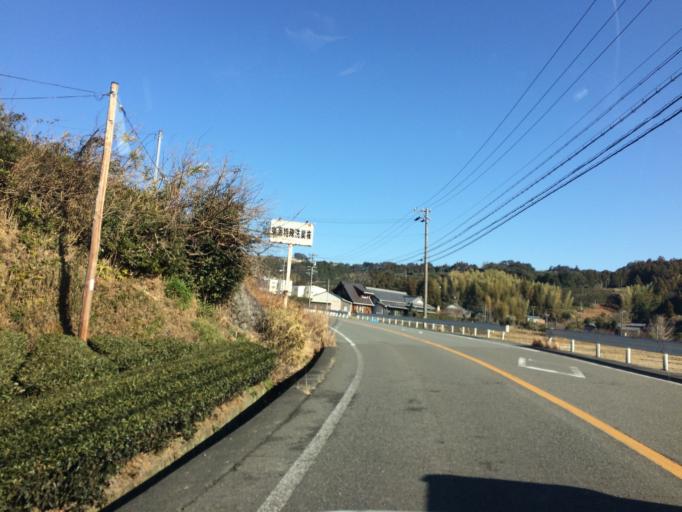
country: JP
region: Shizuoka
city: Shimada
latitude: 34.8490
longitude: 138.2026
